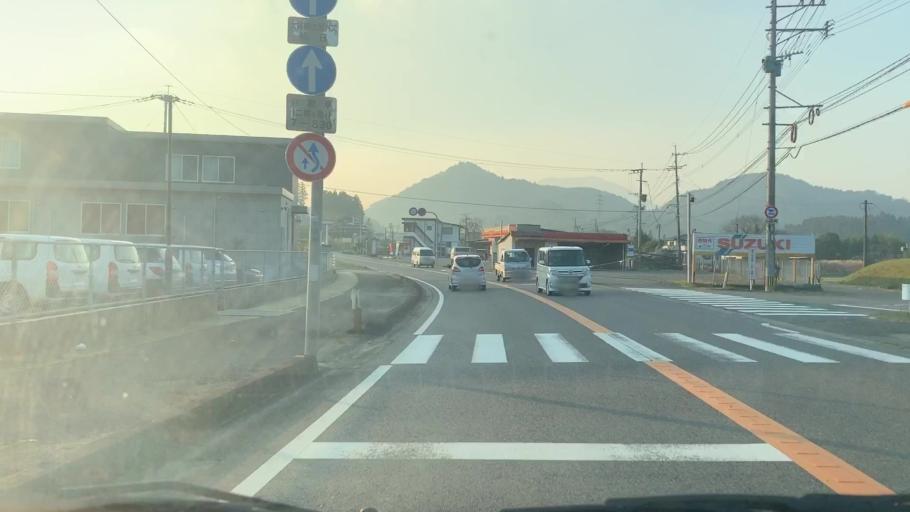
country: JP
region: Saga Prefecture
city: Takeocho-takeo
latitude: 33.2728
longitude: 130.1195
